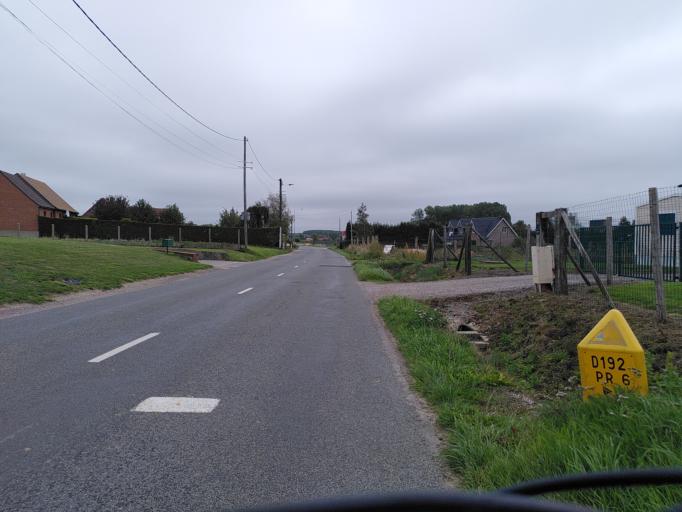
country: FR
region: Nord-Pas-de-Calais
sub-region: Departement du Pas-de-Calais
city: Mametz
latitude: 50.6453
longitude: 2.3117
